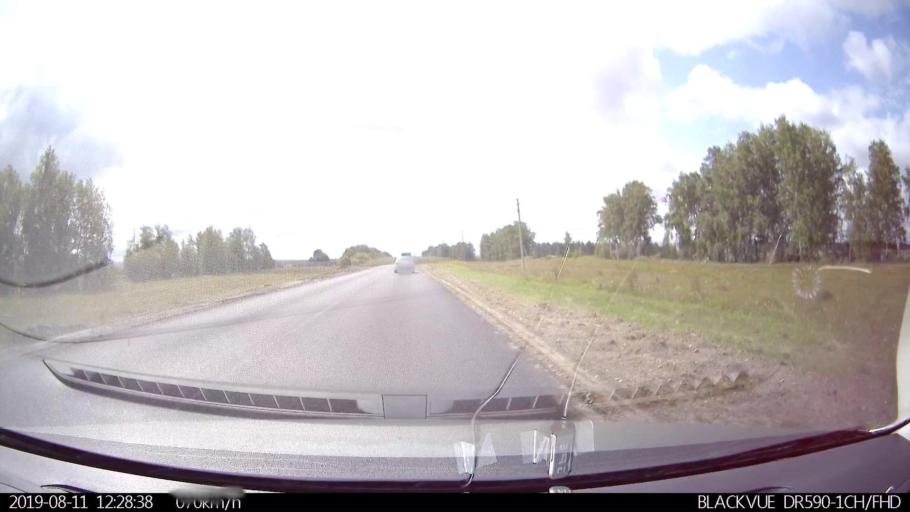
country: RU
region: Ulyanovsk
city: Ignatovka
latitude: 53.8419
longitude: 47.9100
